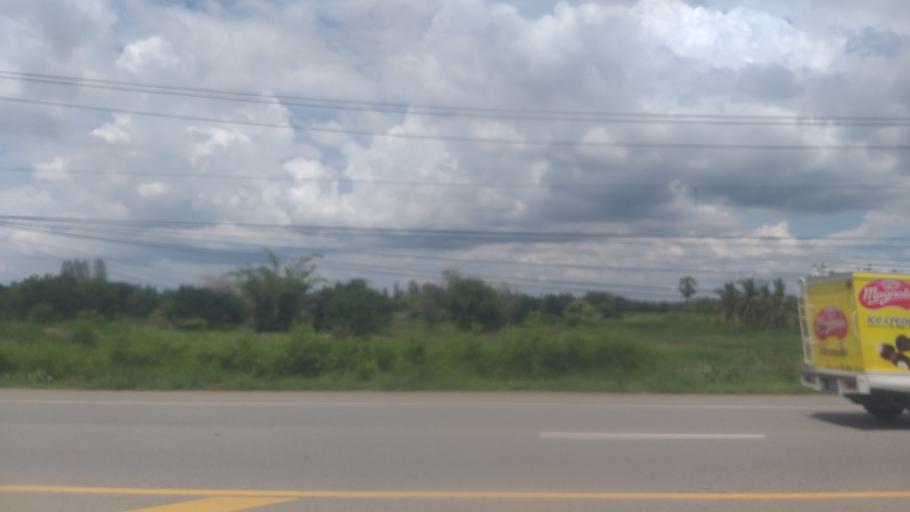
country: TH
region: Nakhon Ratchasima
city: Non Thai
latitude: 15.1330
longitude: 102.1042
